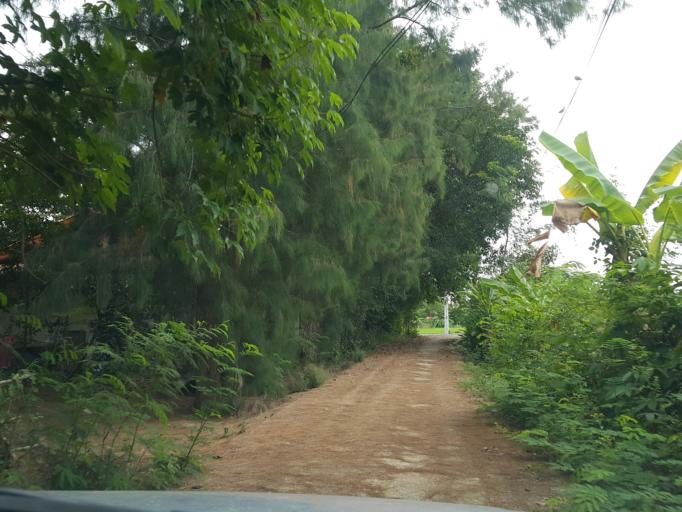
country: TH
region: Chiang Mai
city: San Kamphaeng
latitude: 18.8146
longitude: 99.1259
